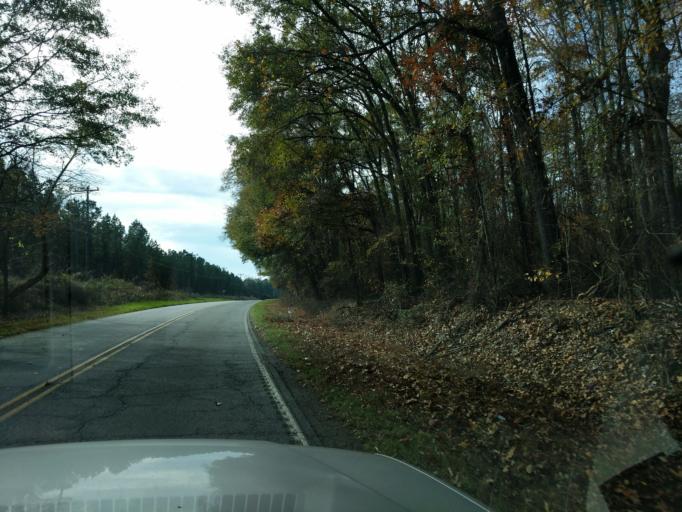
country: US
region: South Carolina
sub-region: Spartanburg County
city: Woodruff
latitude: 34.6466
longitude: -81.9637
